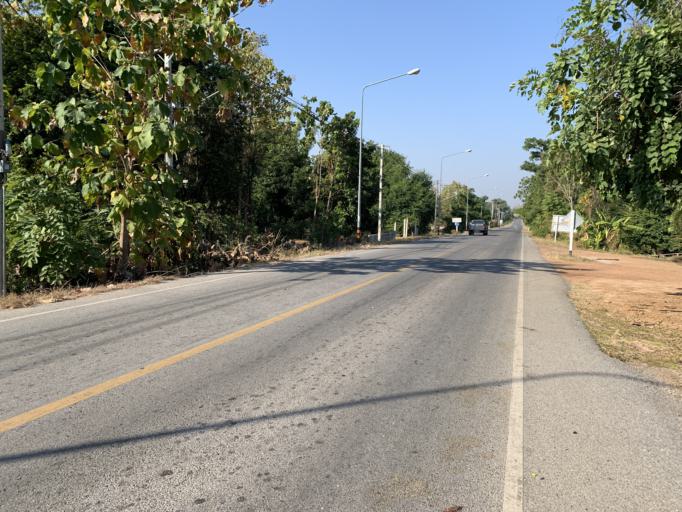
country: TH
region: Uttaradit
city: Thong Saen Khan
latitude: 17.5205
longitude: 100.2592
